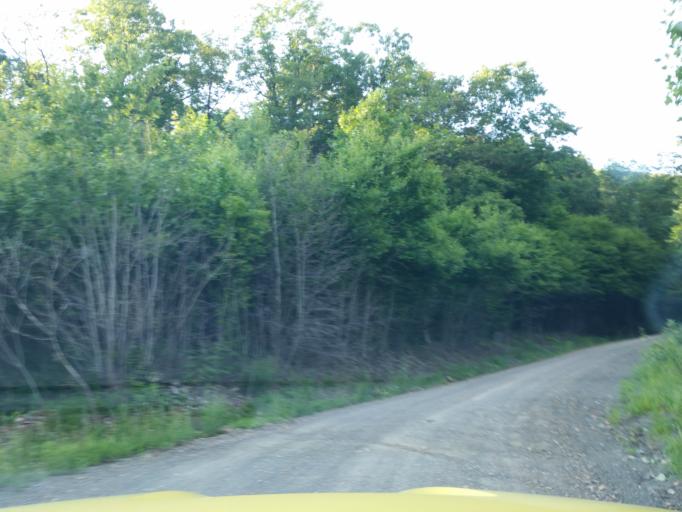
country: US
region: Pennsylvania
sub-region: Dauphin County
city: Williamstown
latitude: 40.4630
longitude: -76.6290
